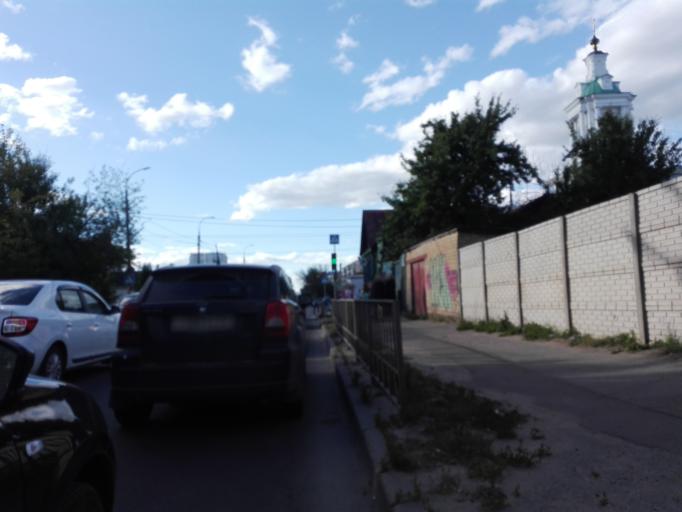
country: RU
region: Orjol
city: Orel
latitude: 52.9535
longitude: 36.0744
